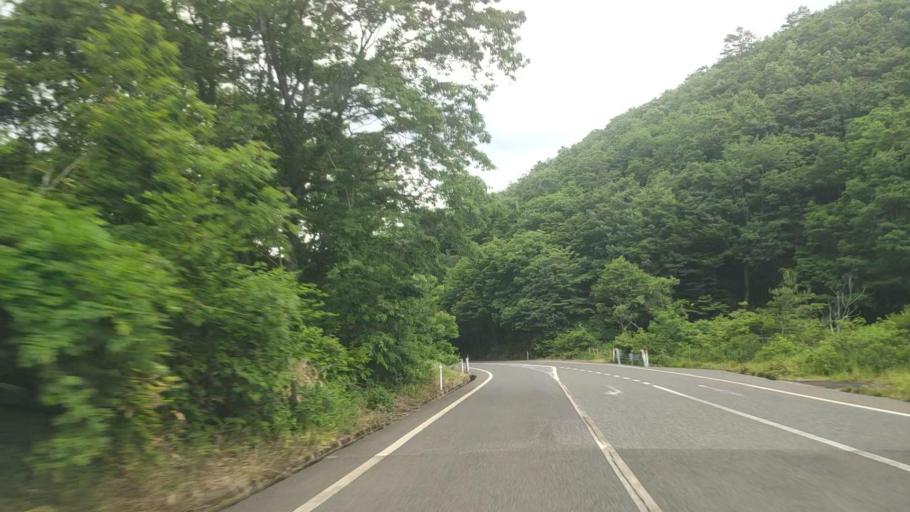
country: JP
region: Tottori
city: Kurayoshi
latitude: 35.2933
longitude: 133.9915
